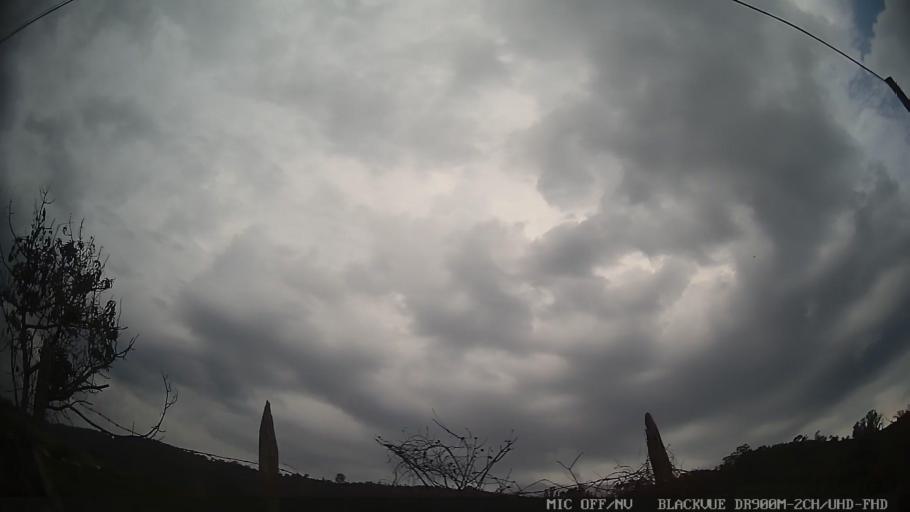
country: BR
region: Sao Paulo
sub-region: Itatiba
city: Itatiba
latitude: -23.0175
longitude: -46.8977
